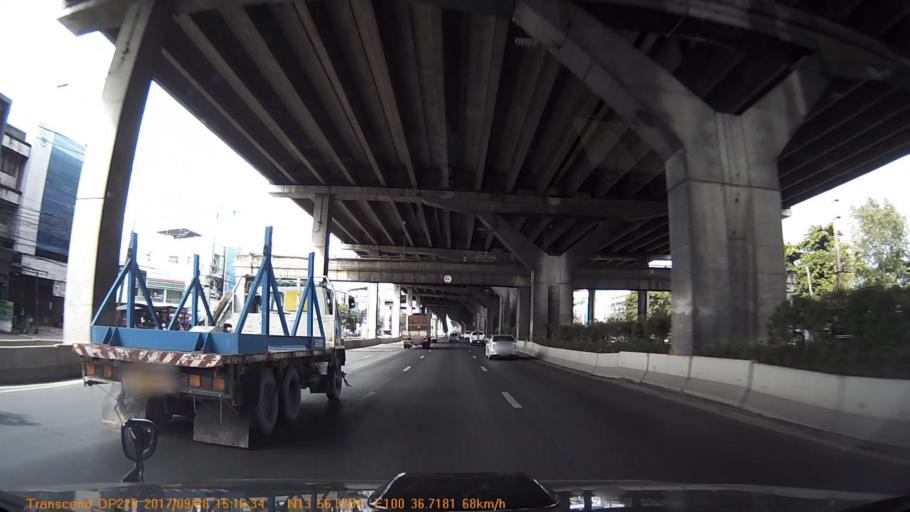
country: TH
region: Bangkok
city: Don Mueang
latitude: 13.9390
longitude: 100.6121
